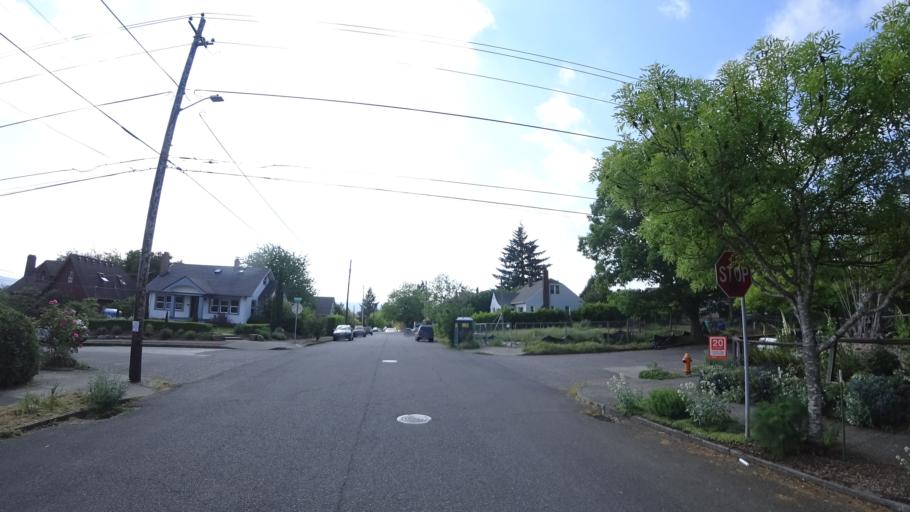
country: US
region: Oregon
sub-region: Multnomah County
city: Portland
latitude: 45.5544
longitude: -122.6470
